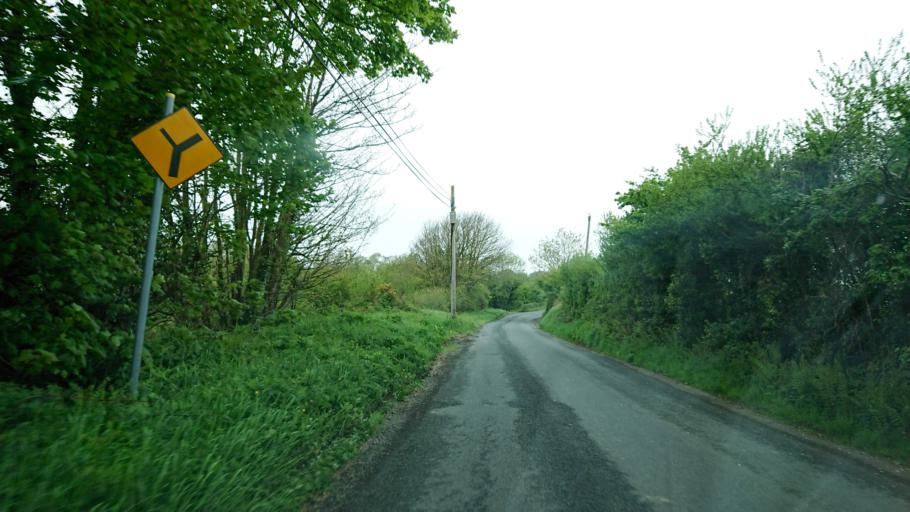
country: IE
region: Munster
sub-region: Waterford
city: Waterford
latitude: 52.2256
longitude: -7.0352
